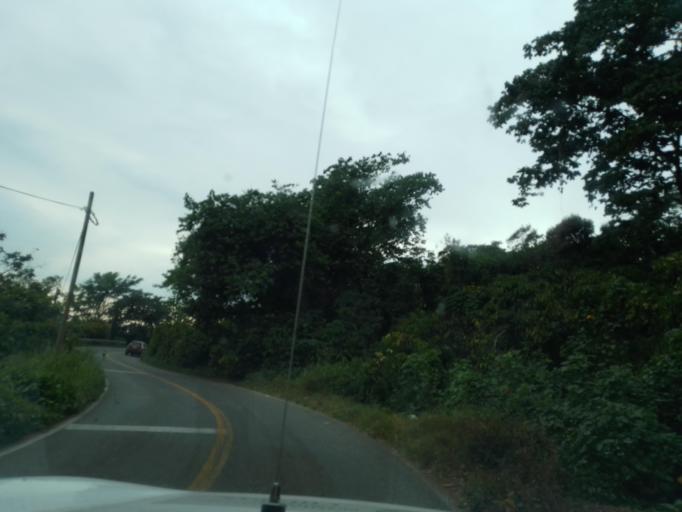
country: MX
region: Chiapas
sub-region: Union Juarez
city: Santo Domingo
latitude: 15.0373
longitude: -92.1209
